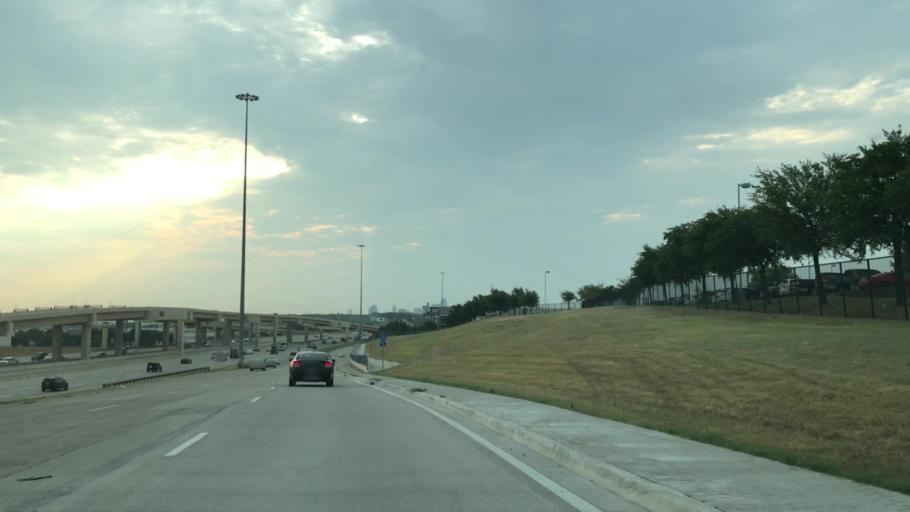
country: US
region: Texas
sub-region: Dallas County
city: Cockrell Hill
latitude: 32.7662
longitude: -96.8940
